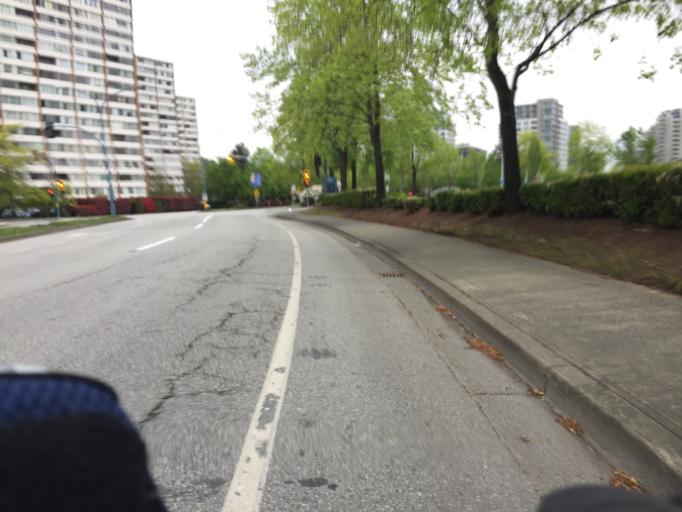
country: CA
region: British Columbia
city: Richmond
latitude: 49.1645
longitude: -123.1402
